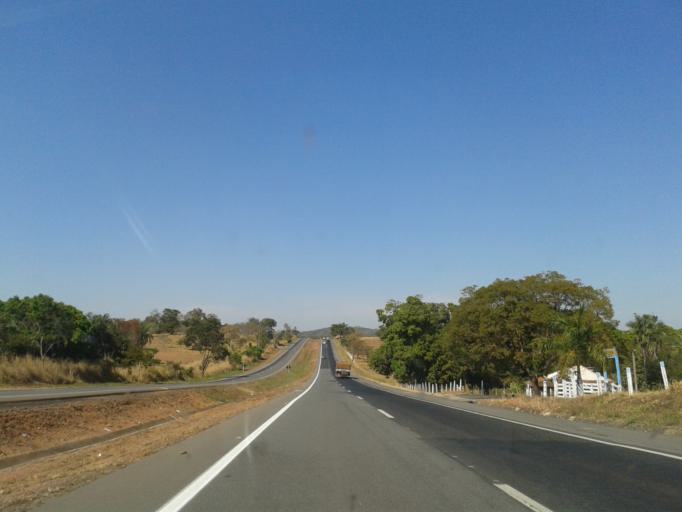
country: BR
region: Goias
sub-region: Piracanjuba
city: Piracanjuba
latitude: -17.3171
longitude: -49.2391
